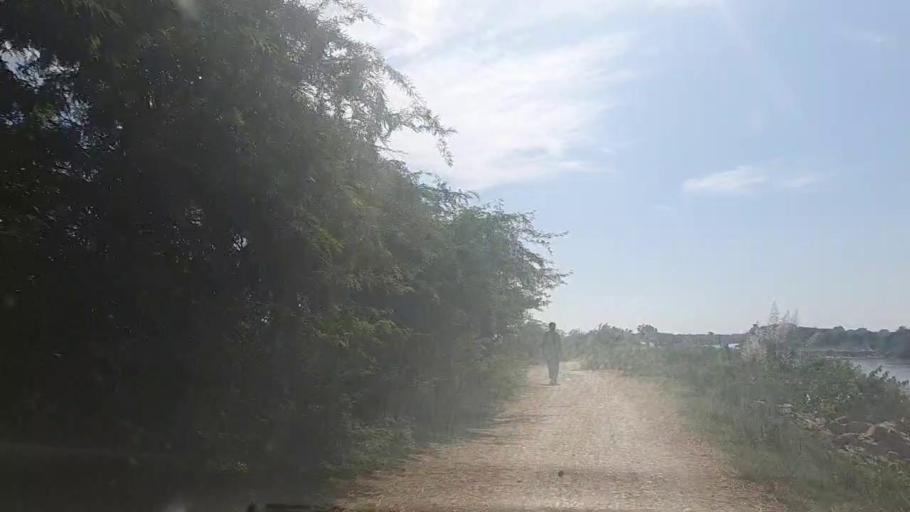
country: PK
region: Sindh
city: Mirpur Batoro
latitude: 24.6825
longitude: 68.1810
